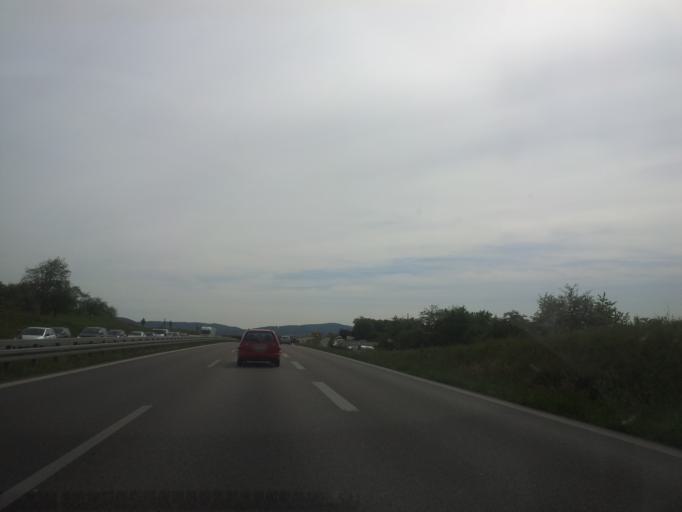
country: DE
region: Baden-Wuerttemberg
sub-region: Regierungsbezirk Stuttgart
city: Leutenbach
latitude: 48.9040
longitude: 9.4219
